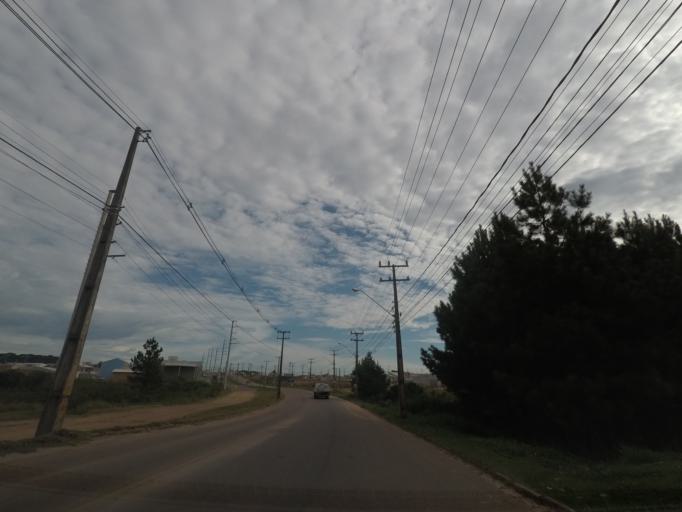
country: BR
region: Parana
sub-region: Araucaria
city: Araucaria
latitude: -25.6308
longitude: -49.2896
